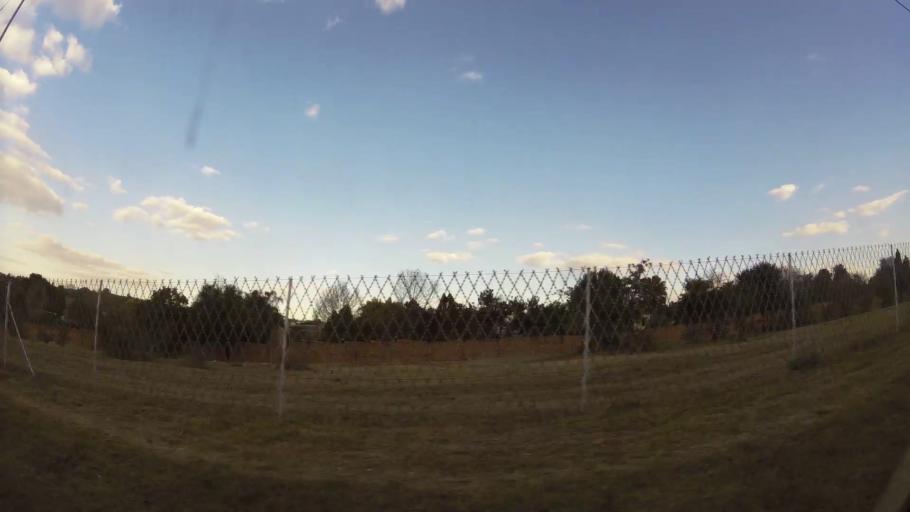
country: ZA
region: Gauteng
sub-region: City of Johannesburg Metropolitan Municipality
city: Diepsloot
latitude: -25.9995
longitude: 28.0032
